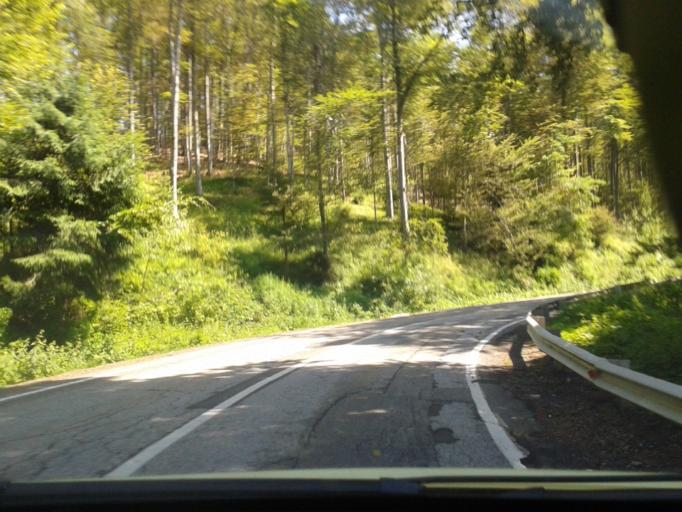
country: RO
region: Sibiu
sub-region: Comuna Cartisoara
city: Cartisoara
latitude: 45.6756
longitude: 24.5895
